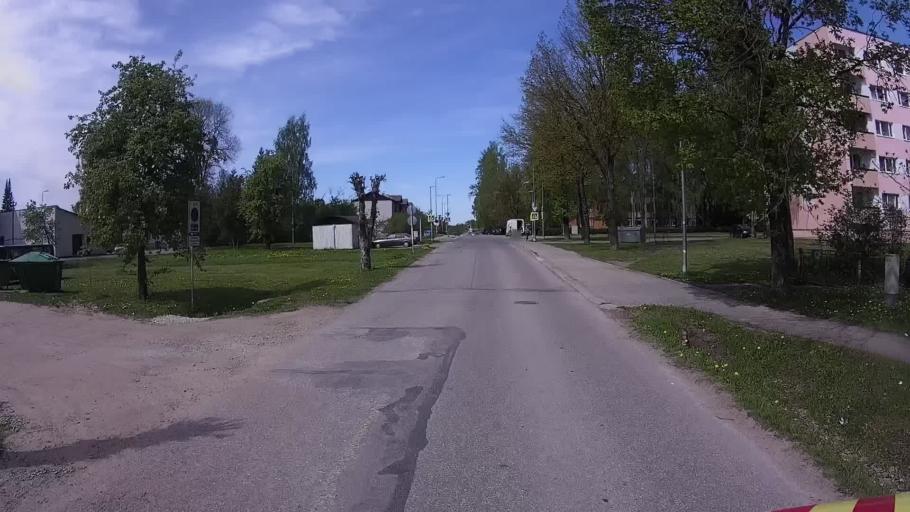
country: EE
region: Valgamaa
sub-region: Valga linn
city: Valga
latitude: 57.7820
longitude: 26.0616
